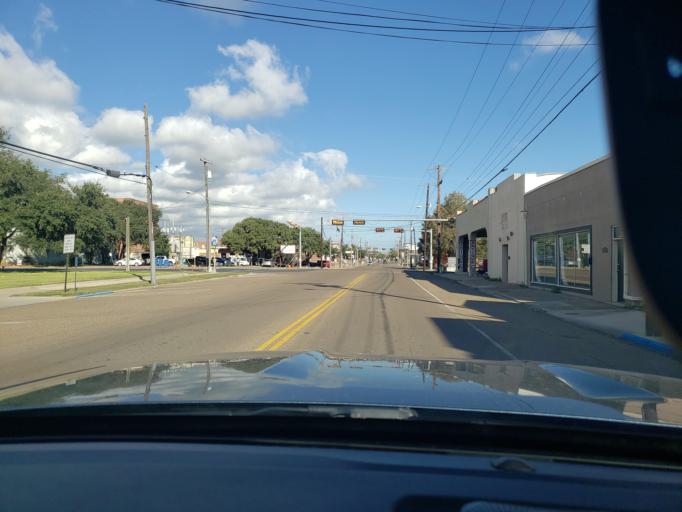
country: US
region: Texas
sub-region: Bee County
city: Beeville
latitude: 28.4015
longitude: -97.7478
